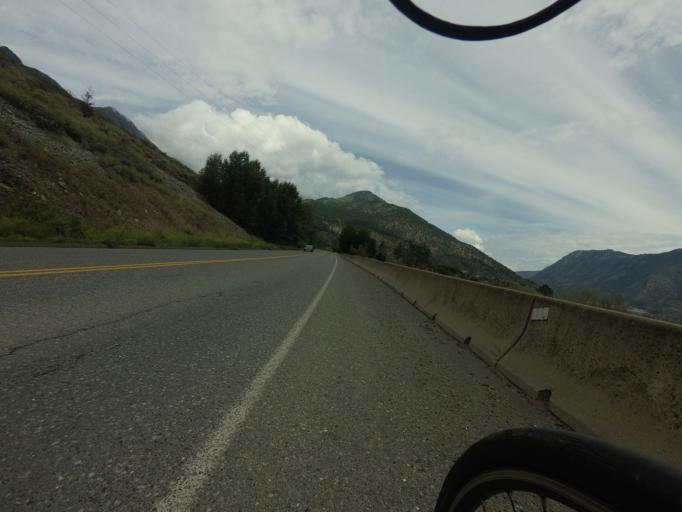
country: CA
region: British Columbia
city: Lillooet
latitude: 50.6828
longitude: -121.9330
